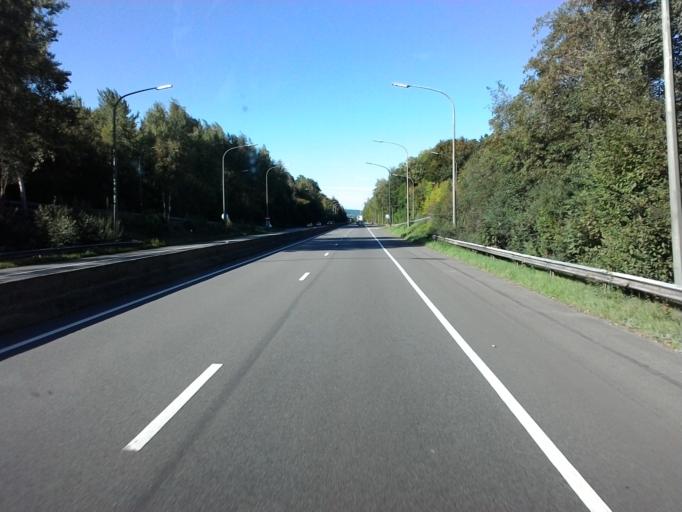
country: BE
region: Wallonia
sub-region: Province du Luxembourg
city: Messancy
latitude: 49.5879
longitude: 5.8087
